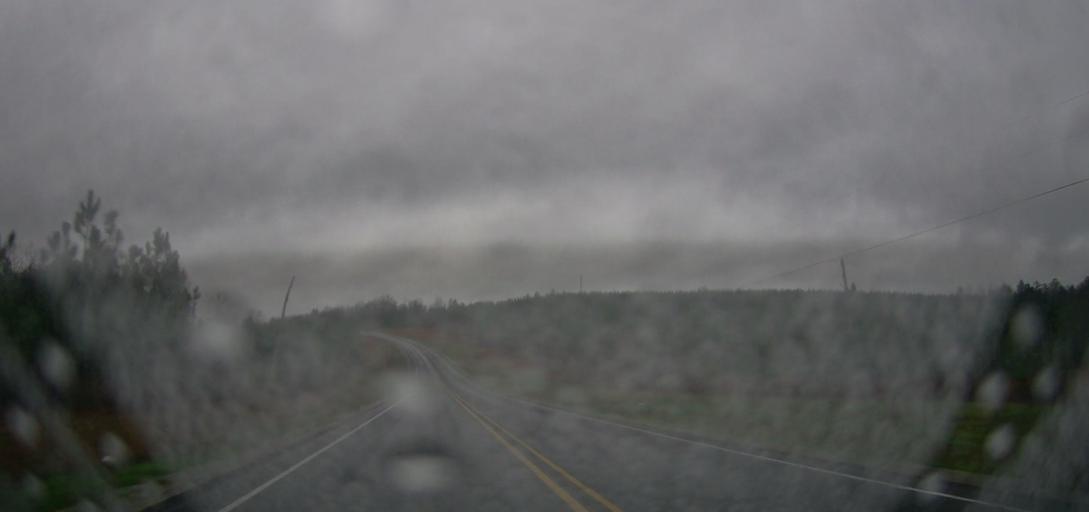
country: US
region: Alabama
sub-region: Chilton County
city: Clanton
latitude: 32.6489
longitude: -86.7644
